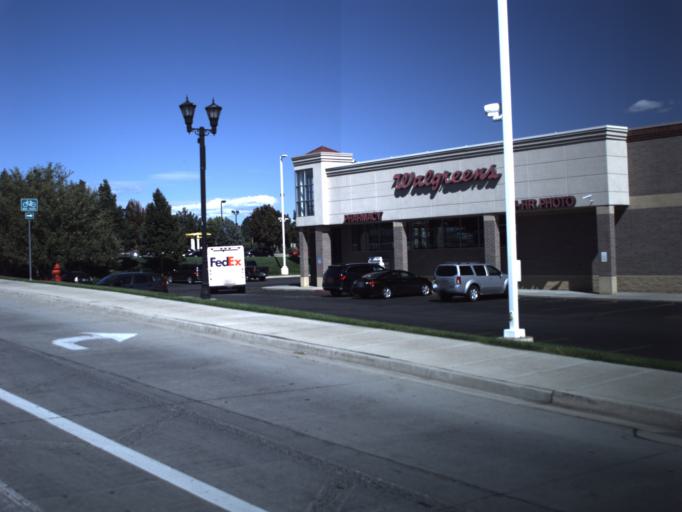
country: US
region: Utah
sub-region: Salt Lake County
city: South Jordan
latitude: 40.5614
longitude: -111.9386
